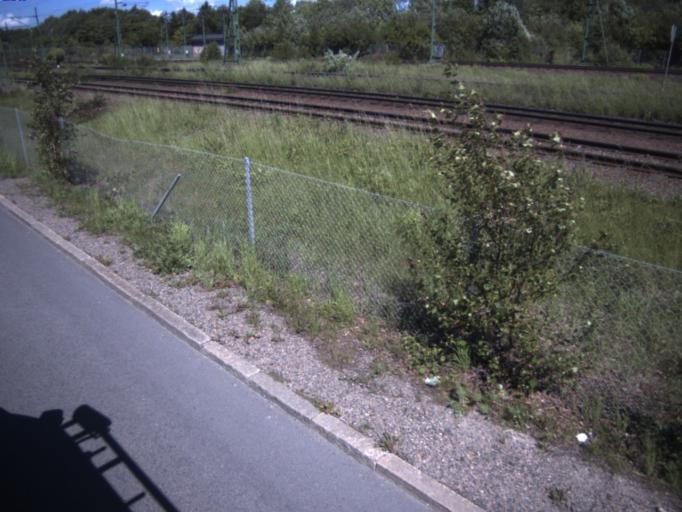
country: SE
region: Skane
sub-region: Helsingborg
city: Helsingborg
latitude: 56.0202
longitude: 12.7316
